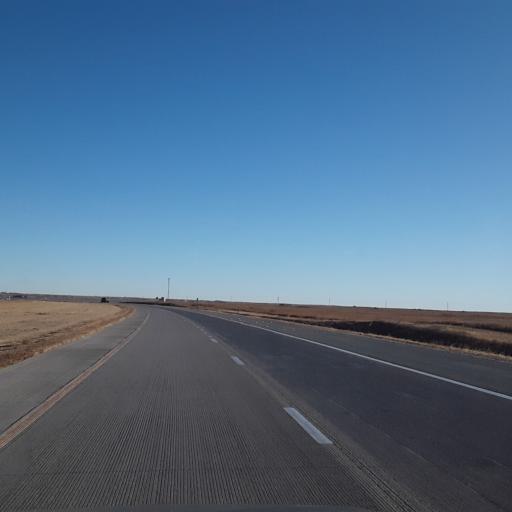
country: US
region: Kansas
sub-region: Seward County
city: Liberal
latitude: 37.1133
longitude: -100.7772
